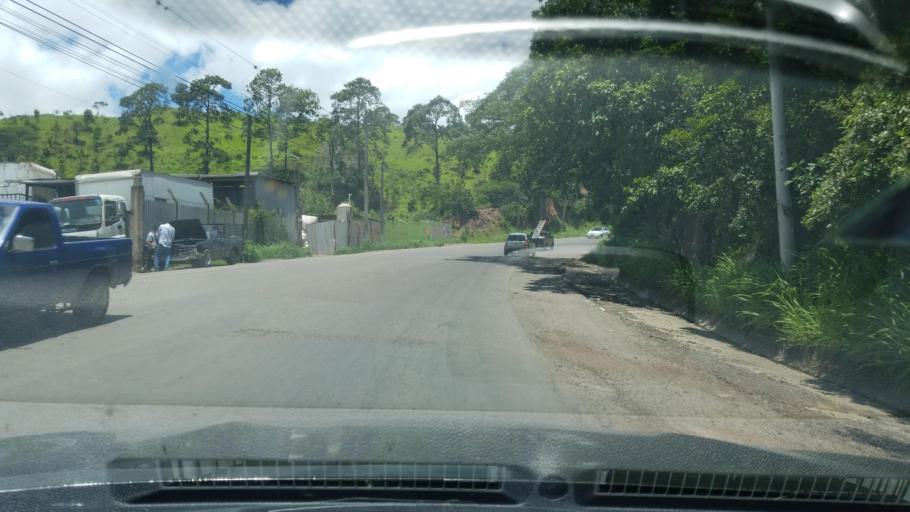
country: HN
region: Francisco Morazan
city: Rio Abajo
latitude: 14.1406
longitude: -87.2302
